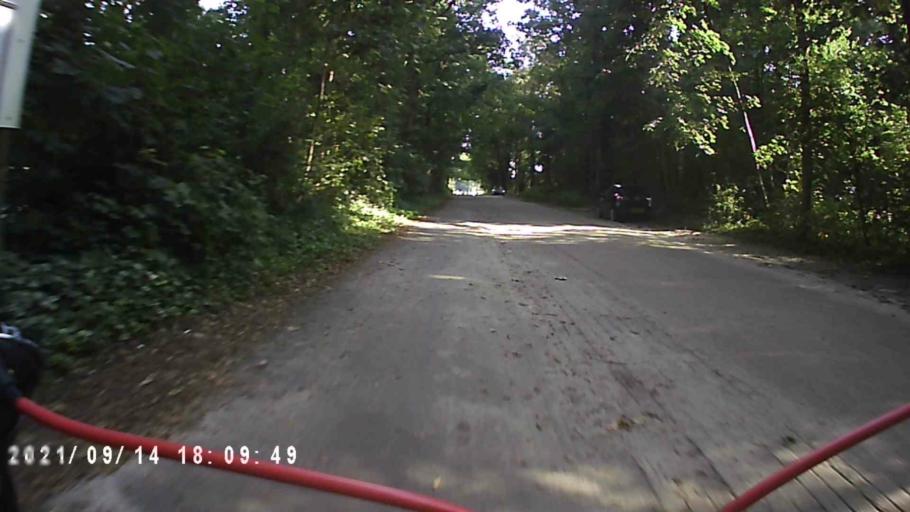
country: NL
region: Drenthe
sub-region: Gemeente Tynaarlo
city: Zuidlaren
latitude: 53.0975
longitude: 6.6554
